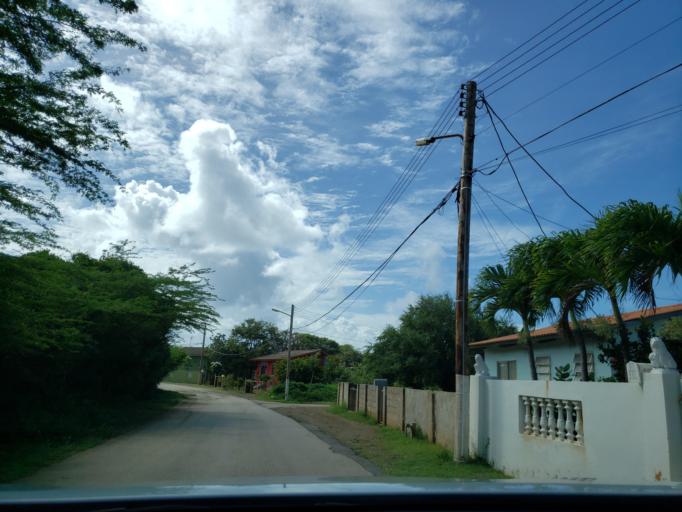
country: CW
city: Dorp Soto
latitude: 12.3717
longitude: -69.1521
